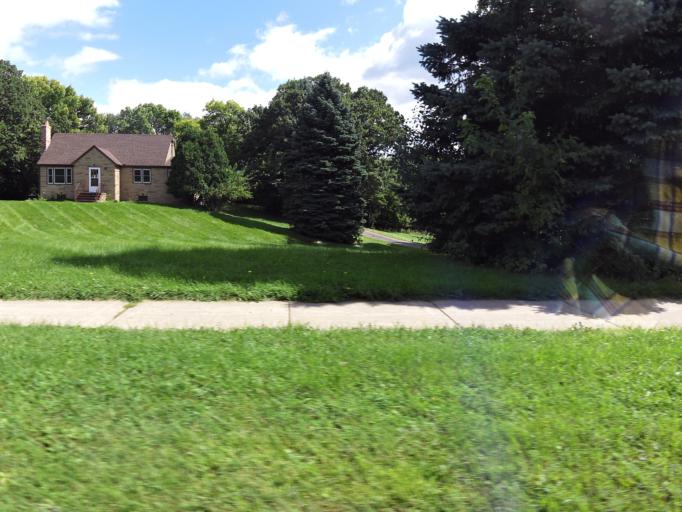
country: US
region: Minnesota
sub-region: Dakota County
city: Inver Grove Heights
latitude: 44.8620
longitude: -93.0449
